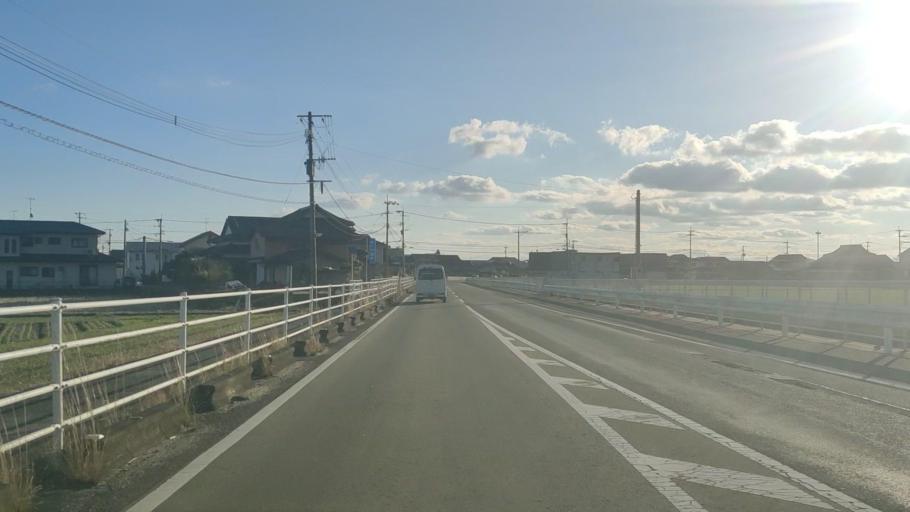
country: JP
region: Saga Prefecture
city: Saga-shi
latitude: 33.2780
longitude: 130.2231
